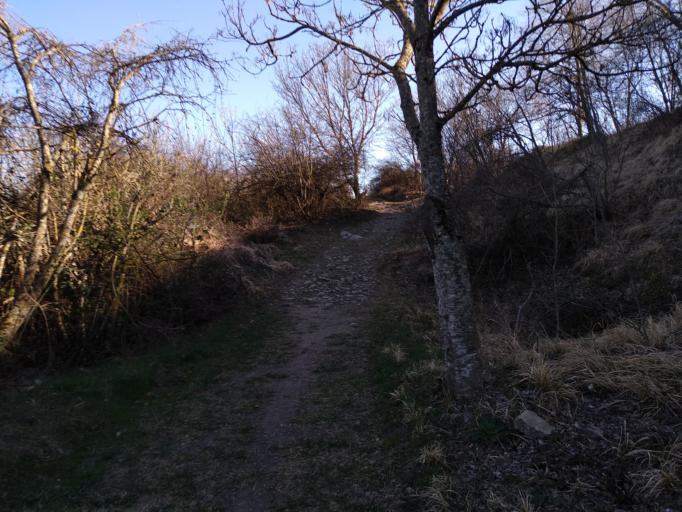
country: IT
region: Emilia-Romagna
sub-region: Provincia di Reggio Emilia
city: Castelnovo ne'Monti
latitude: 44.4263
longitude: 10.4198
